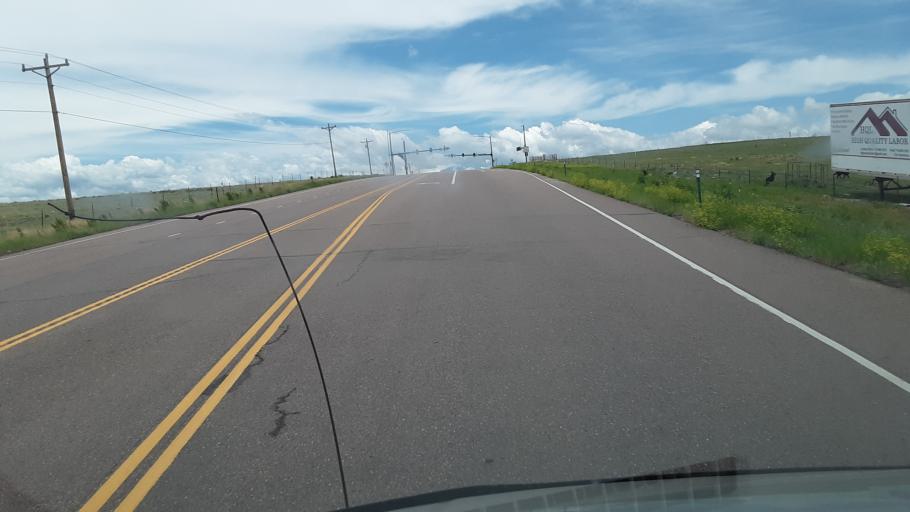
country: US
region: Colorado
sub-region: El Paso County
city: Cimarron Hills
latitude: 38.8387
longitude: -104.5509
